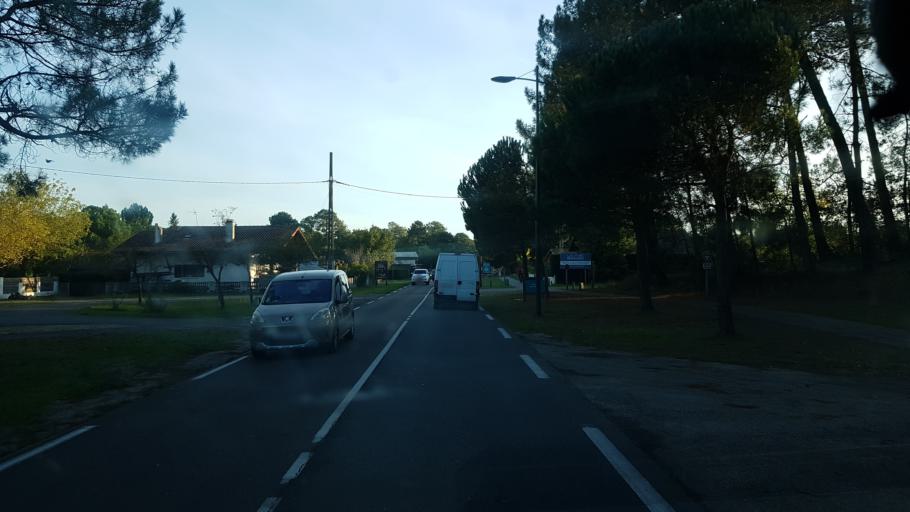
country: FR
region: Aquitaine
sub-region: Departement de la Gironde
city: Ares
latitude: 44.7575
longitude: -1.1801
